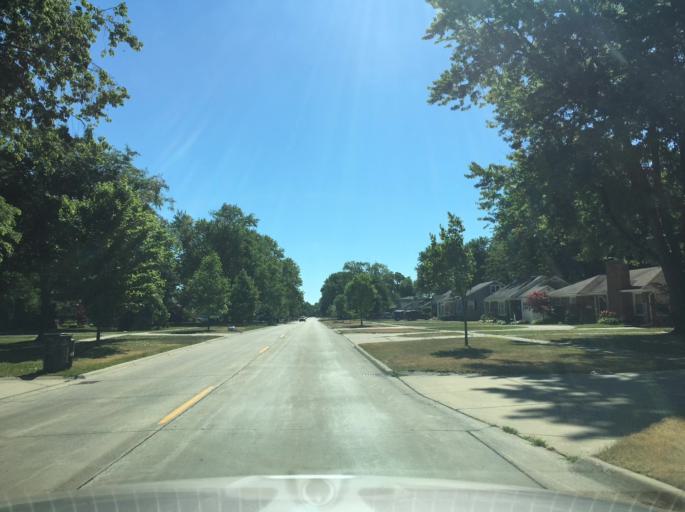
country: US
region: Michigan
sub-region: Macomb County
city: Saint Clair Shores
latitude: 42.5028
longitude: -82.9029
